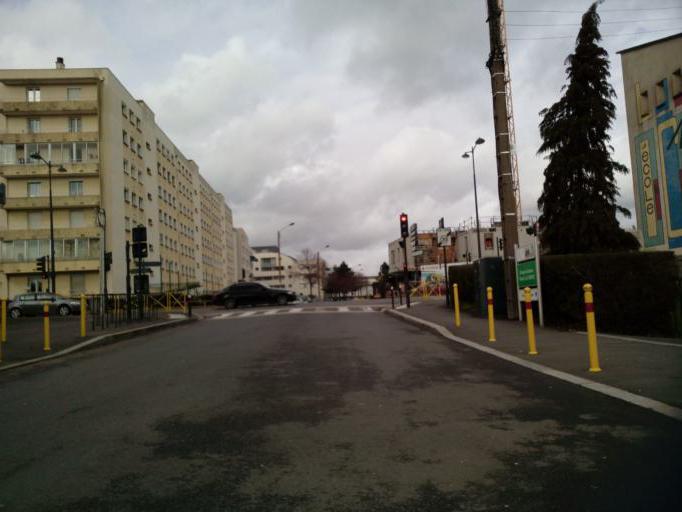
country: FR
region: Brittany
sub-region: Departement d'Ille-et-Vilaine
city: Rennes
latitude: 48.1085
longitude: -1.7101
